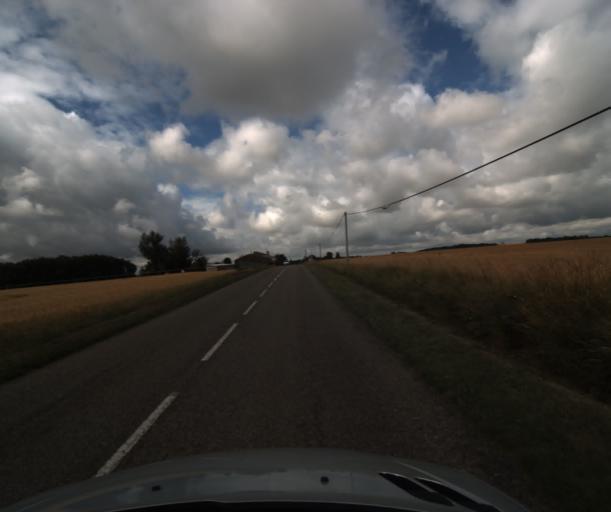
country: FR
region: Midi-Pyrenees
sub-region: Departement du Tarn-et-Garonne
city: Lavit
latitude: 43.9785
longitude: 0.9585
